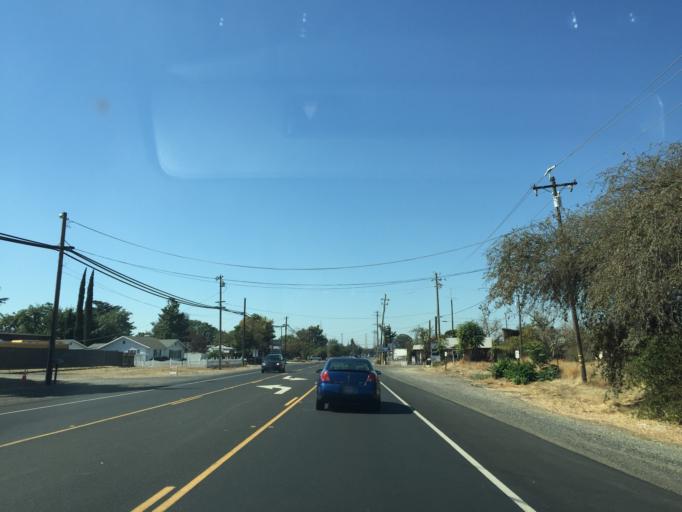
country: US
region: California
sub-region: Stanislaus County
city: East Oakdale
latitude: 37.7758
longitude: -120.8190
